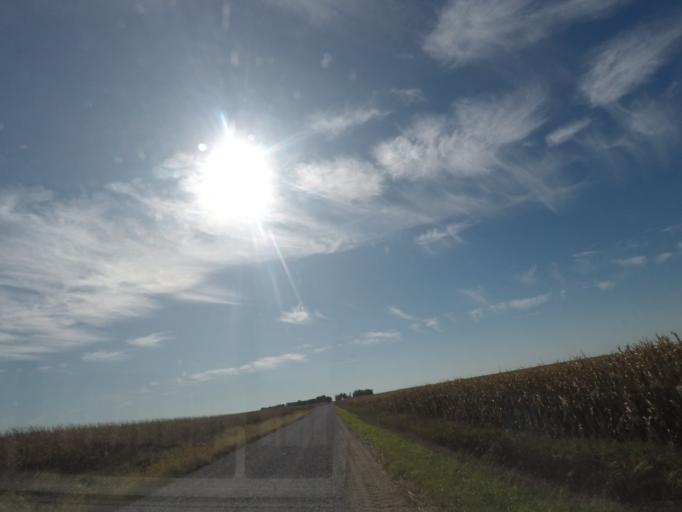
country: US
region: Iowa
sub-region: Story County
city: Nevada
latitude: 42.0587
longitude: -93.3288
